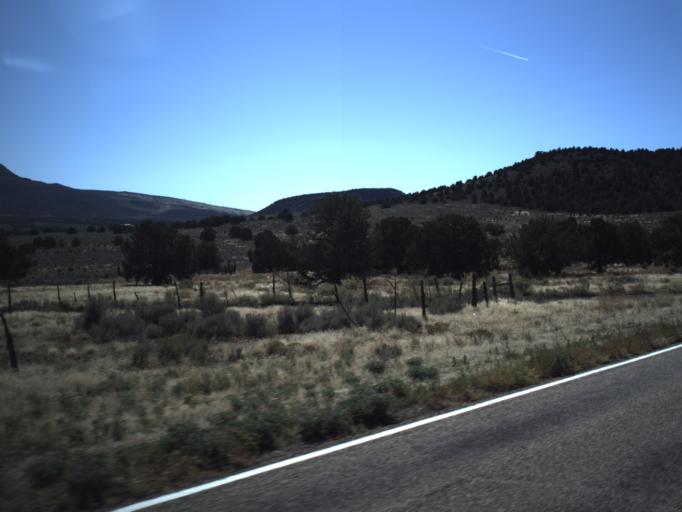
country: US
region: Utah
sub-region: Washington County
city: Enterprise
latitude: 37.4030
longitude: -113.6387
